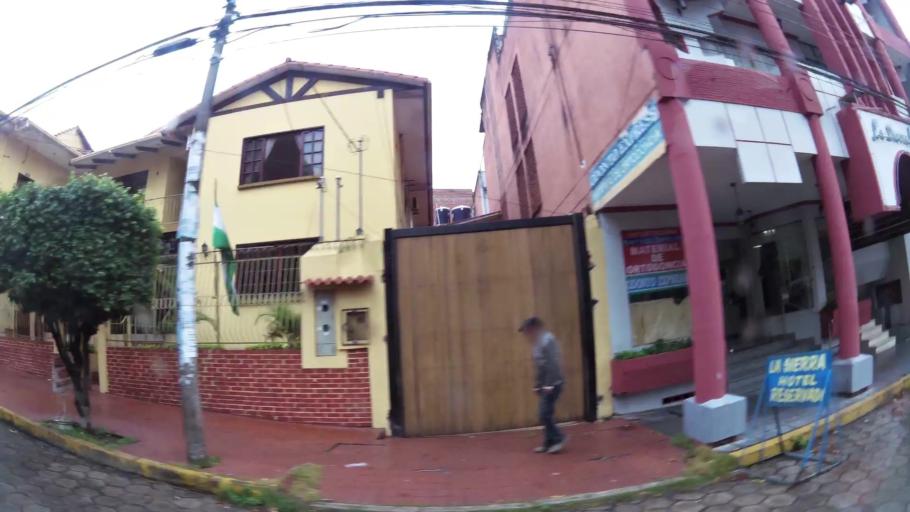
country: BO
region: Santa Cruz
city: Santa Cruz de la Sierra
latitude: -17.7902
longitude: -63.1860
